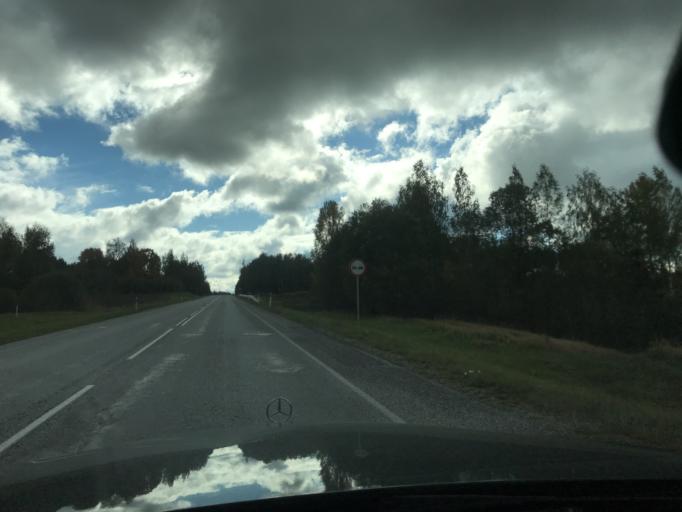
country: RU
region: Pskov
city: Pechory
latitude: 57.7021
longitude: 27.3245
